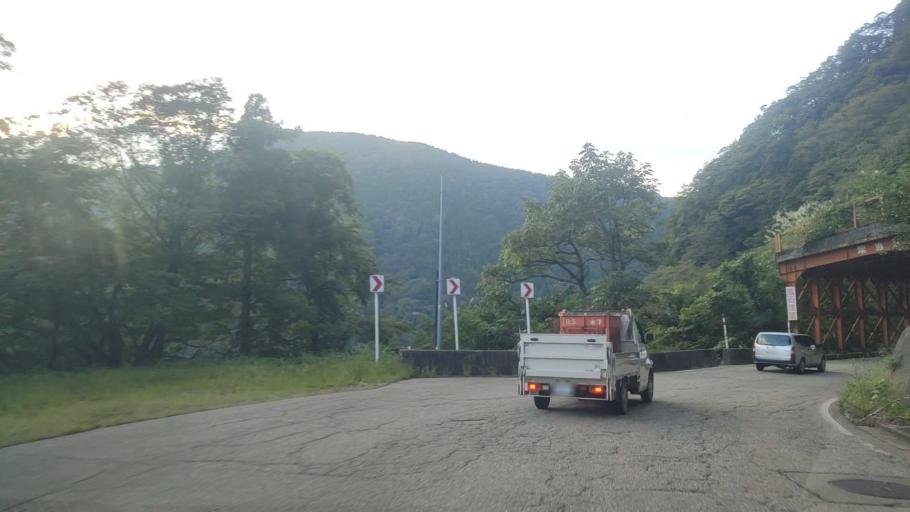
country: JP
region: Toyama
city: Nanto-shi
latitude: 36.5421
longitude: 137.0086
